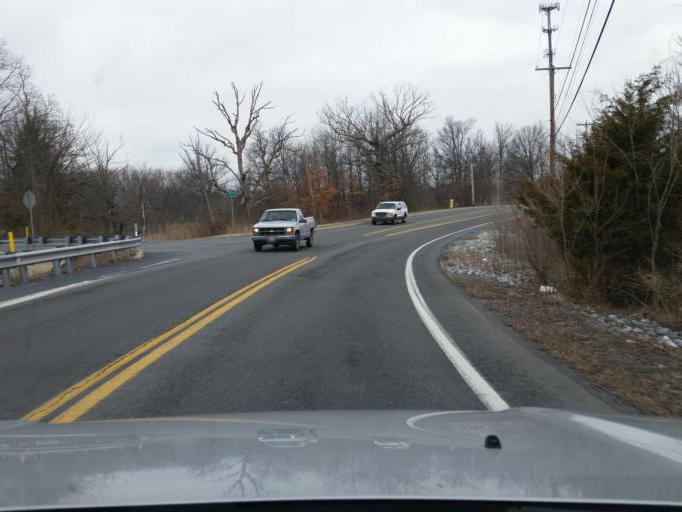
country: US
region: Pennsylvania
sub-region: Dauphin County
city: Paxtonia
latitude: 40.3162
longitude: -76.7786
